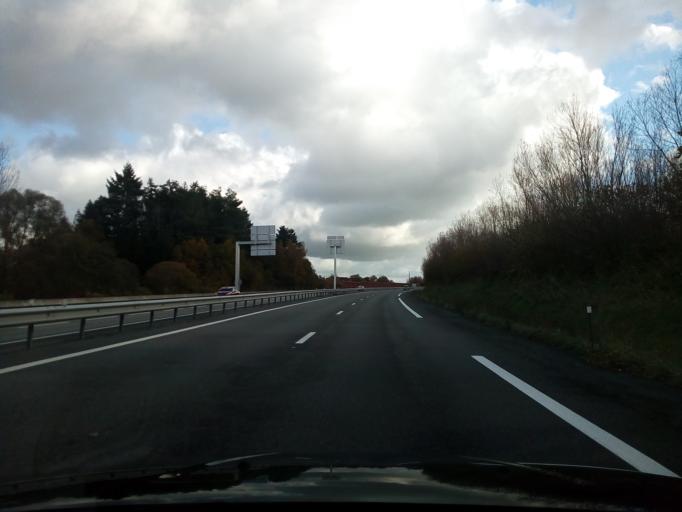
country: FR
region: Limousin
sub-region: Departement de la Creuse
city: Gouzon
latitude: 46.1992
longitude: 2.2420
